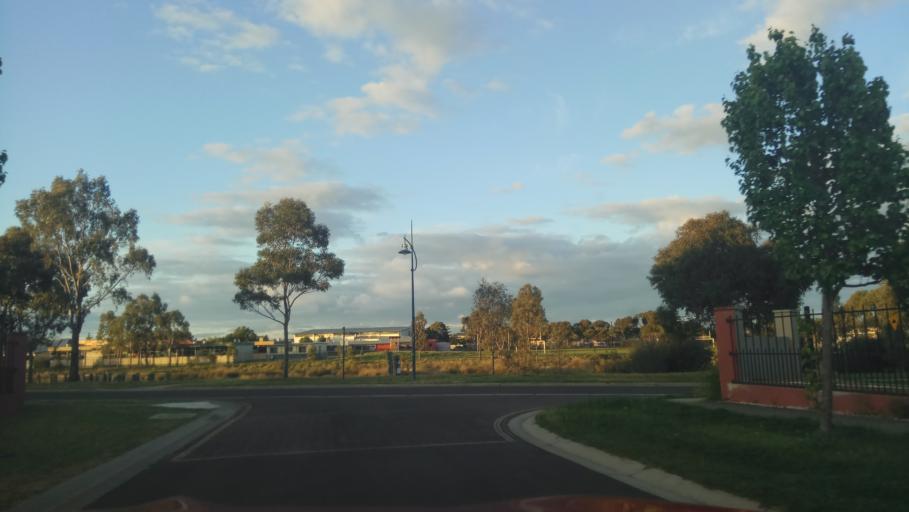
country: AU
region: Victoria
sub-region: Wyndham
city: Point Cook
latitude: -37.8978
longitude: 144.7453
